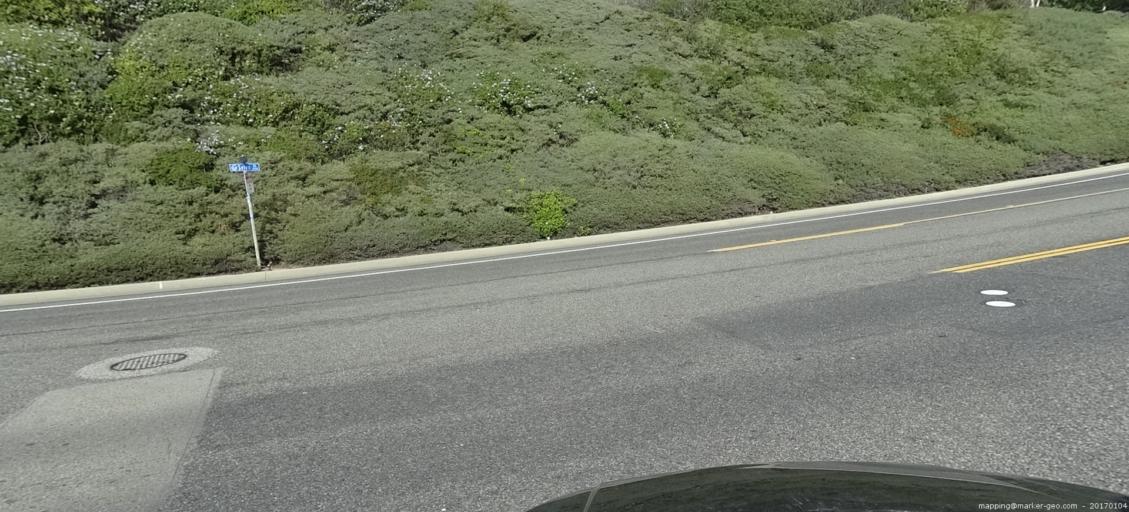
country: US
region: California
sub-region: Orange County
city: Dana Point
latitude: 33.4727
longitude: -117.6955
